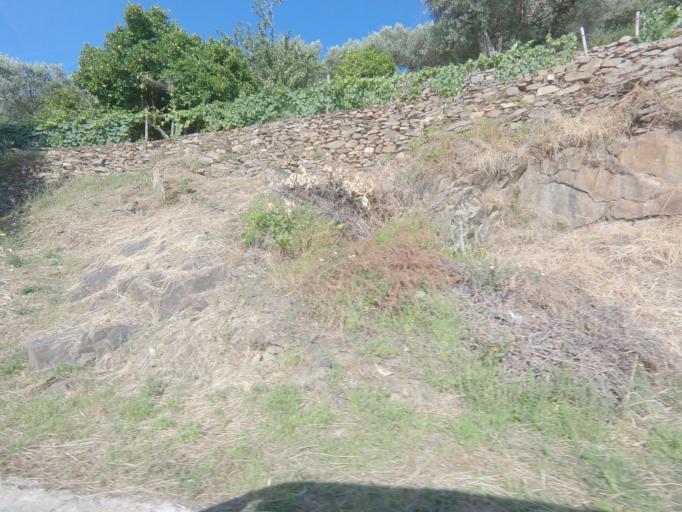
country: PT
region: Vila Real
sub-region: Sabrosa
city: Vilela
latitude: 41.2149
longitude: -7.5525
